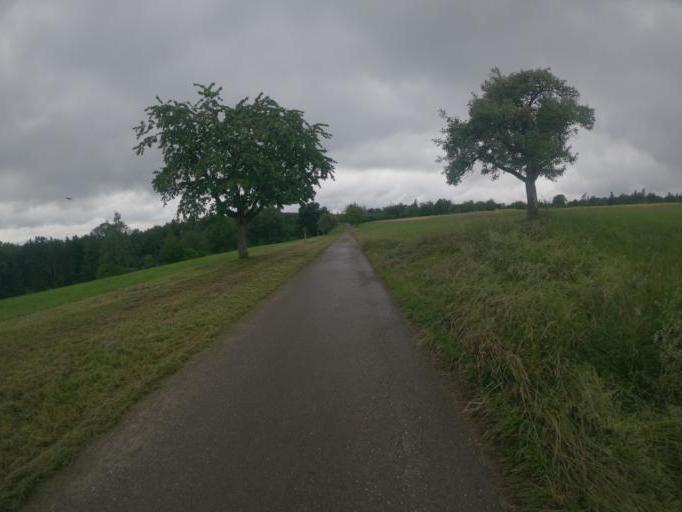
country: DE
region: Baden-Wuerttemberg
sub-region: Regierungsbezirk Stuttgart
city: Schorndorf
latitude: 48.7747
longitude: 9.5444
